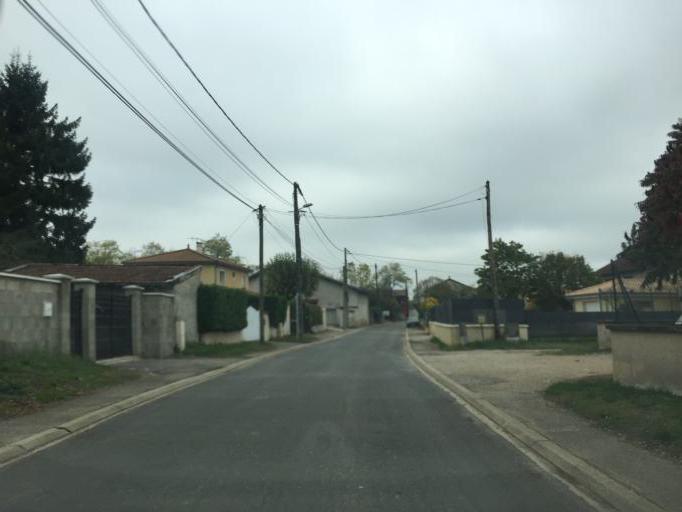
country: FR
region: Rhone-Alpes
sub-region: Departement de l'Ain
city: Nievroz
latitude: 45.8233
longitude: 5.0578
